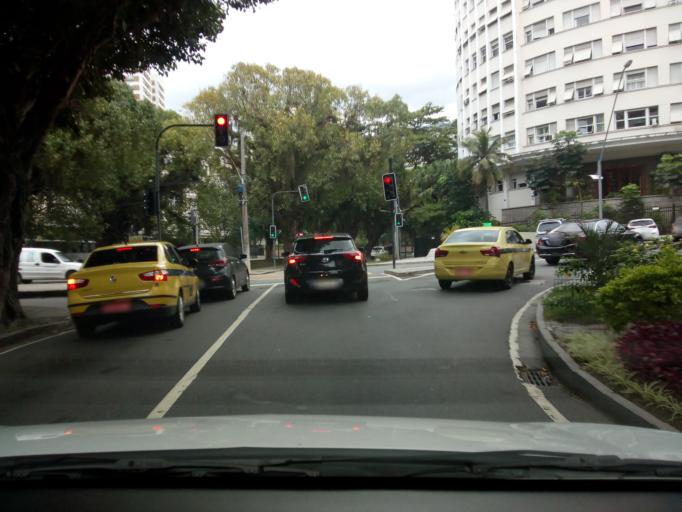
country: BR
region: Rio de Janeiro
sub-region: Rio De Janeiro
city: Rio de Janeiro
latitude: -22.9868
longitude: -43.2291
